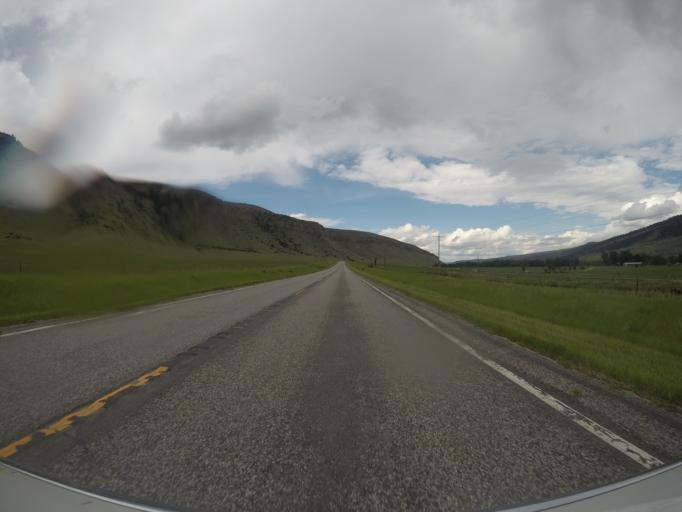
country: US
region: Montana
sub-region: Sweet Grass County
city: Big Timber
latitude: 45.5740
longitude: -110.2000
